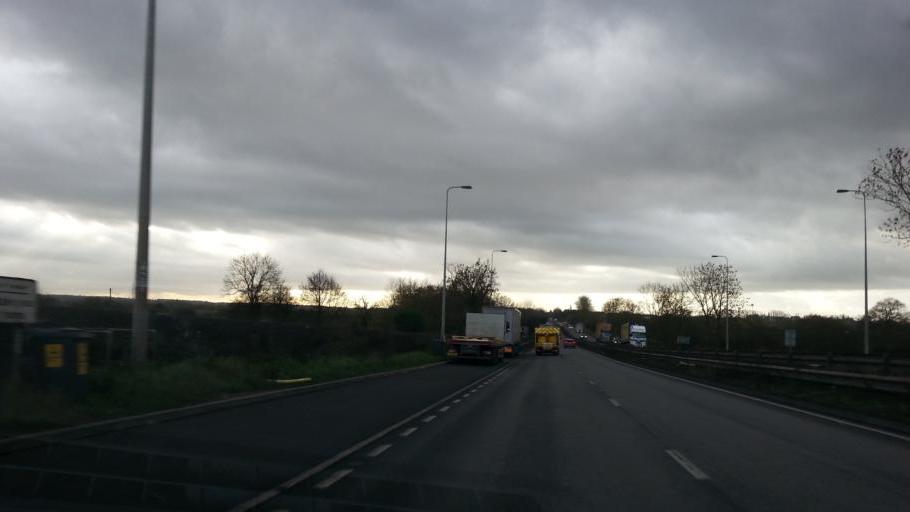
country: GB
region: England
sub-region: Staffordshire
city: Whittington
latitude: 52.7025
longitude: -1.7767
